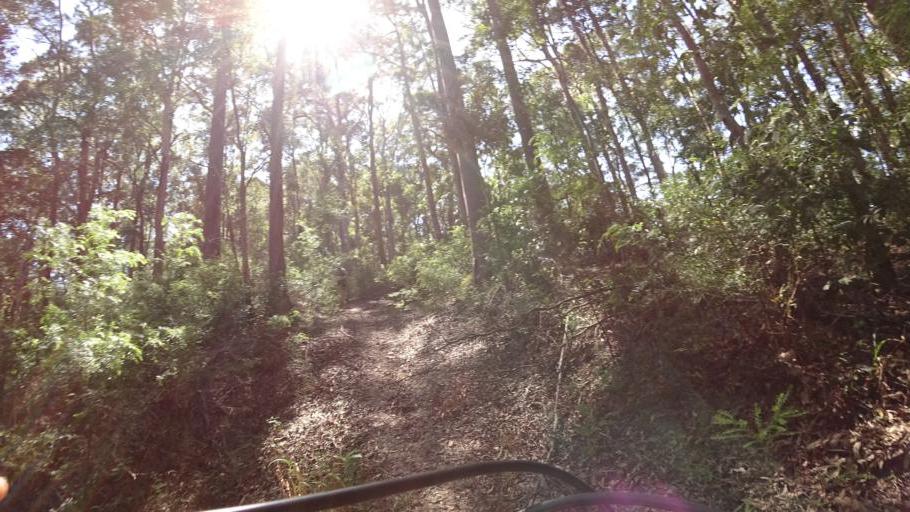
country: AU
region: Queensland
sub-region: Moreton Bay
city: Highvale
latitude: -27.4129
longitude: 152.7903
